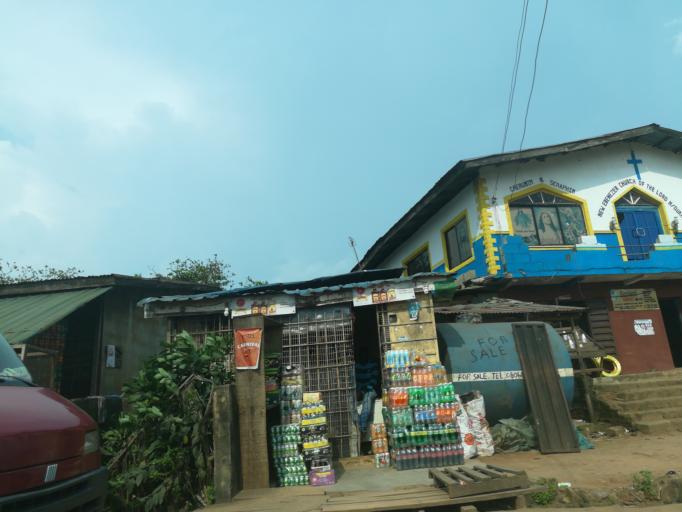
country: NG
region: Lagos
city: Ikorodu
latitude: 6.6693
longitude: 3.6708
